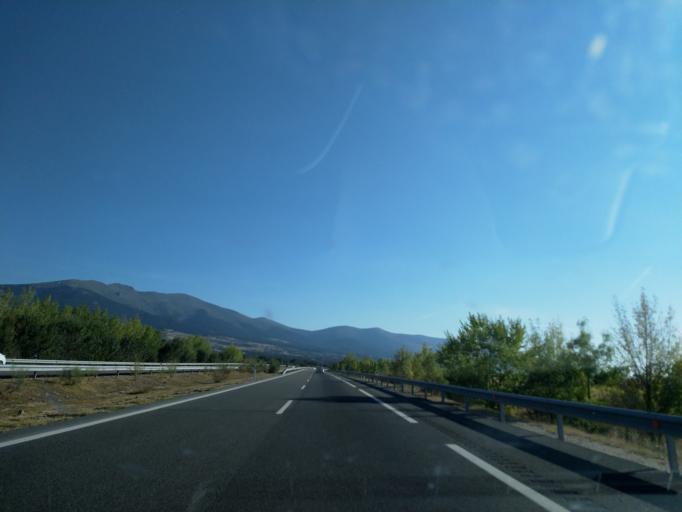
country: ES
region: Castille and Leon
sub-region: Provincia de Segovia
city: Segovia
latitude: 40.8854
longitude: -4.1170
